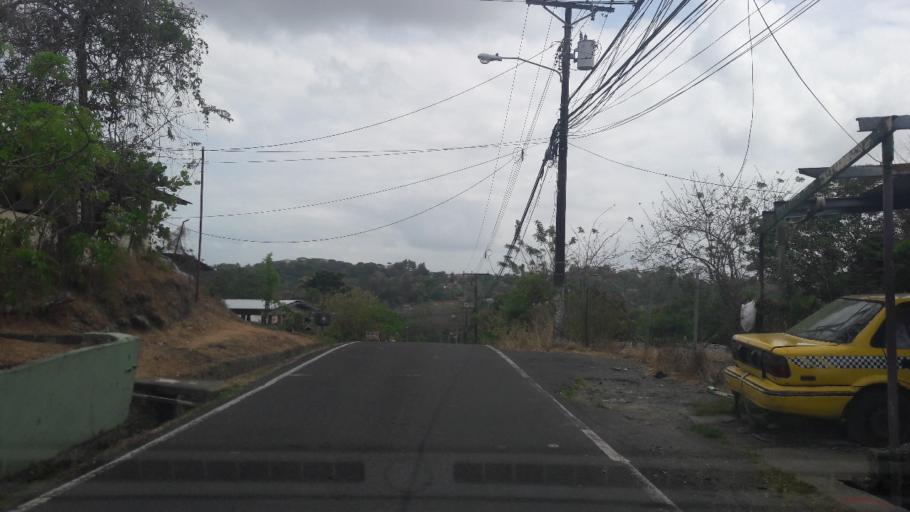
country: PA
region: Panama
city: Alcalde Diaz
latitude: 9.1237
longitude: -79.5469
